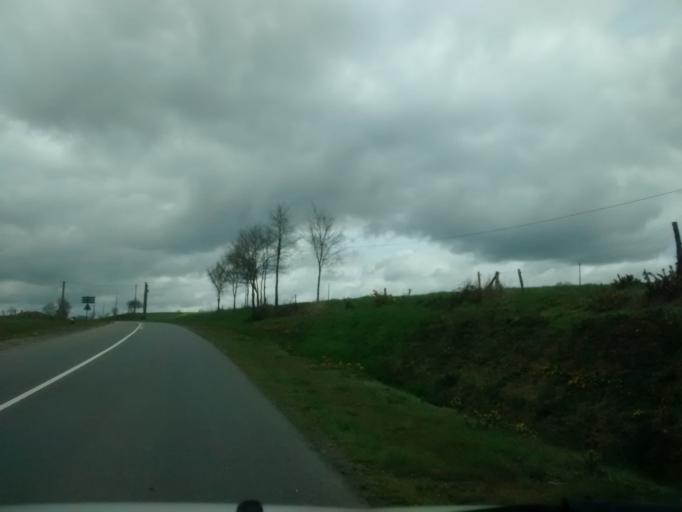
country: FR
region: Brittany
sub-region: Departement d'Ille-et-Vilaine
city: Livre-sur-Changeon
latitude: 48.2316
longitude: -1.3549
